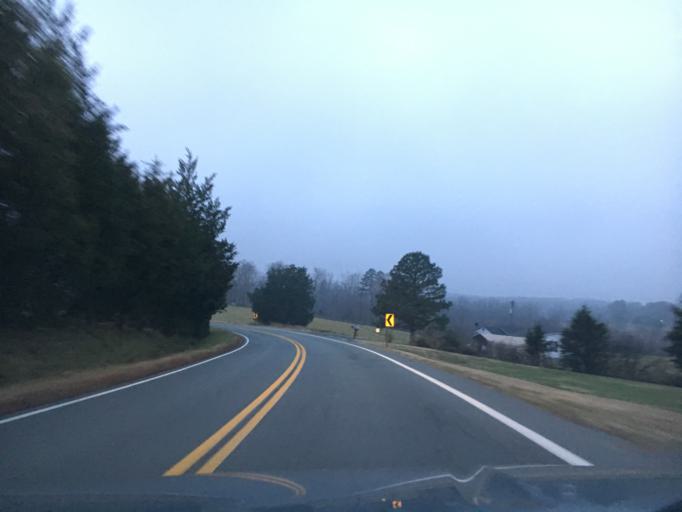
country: US
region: Virginia
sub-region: Halifax County
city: Mountain Road
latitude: 36.7001
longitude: -78.9706
